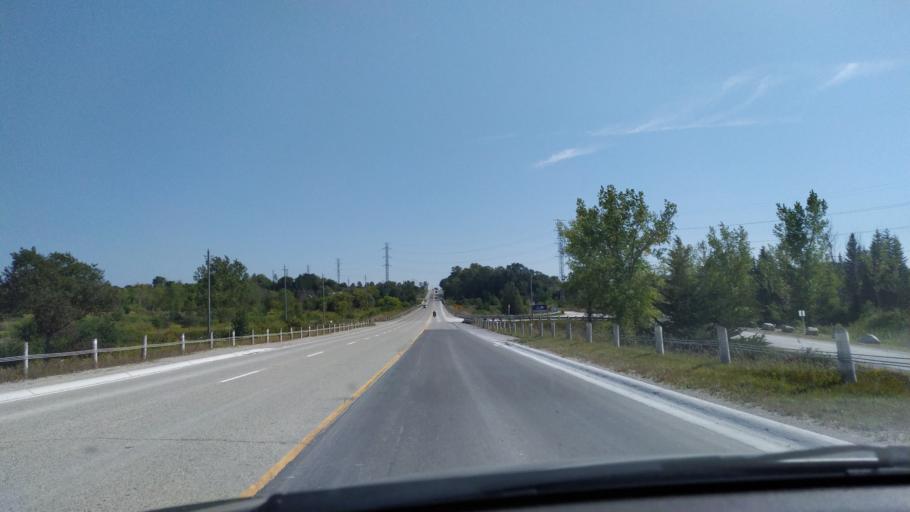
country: CA
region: Ontario
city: Ingersoll
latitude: 43.0713
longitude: -80.8534
